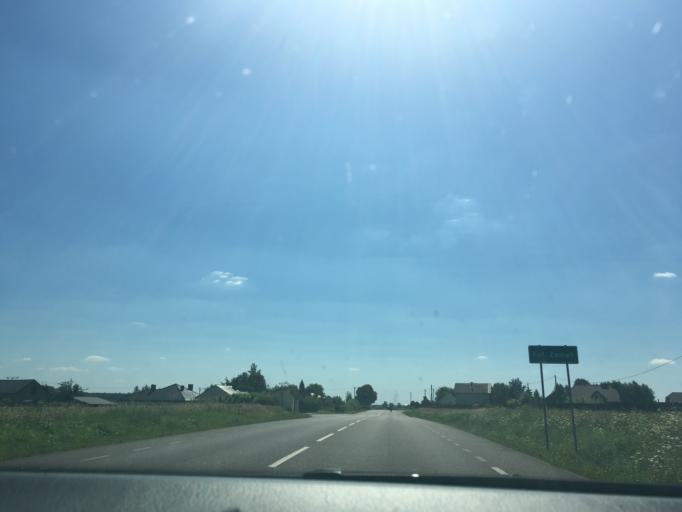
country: PL
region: Lublin Voivodeship
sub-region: Powiat janowski
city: Modliborzyce
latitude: 50.7406
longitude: 22.3474
